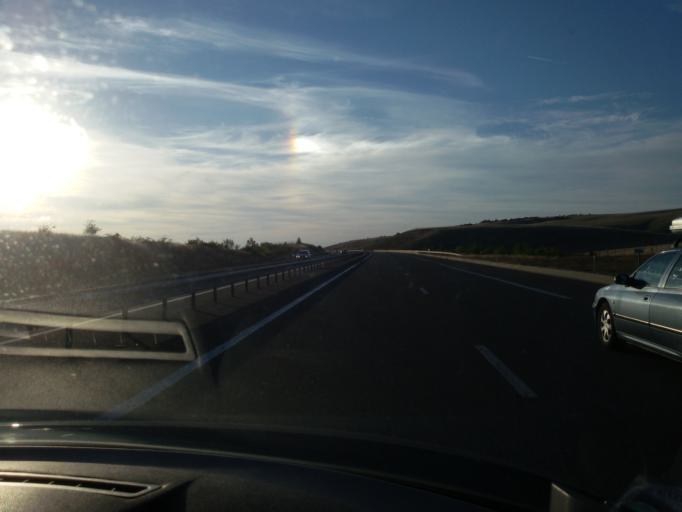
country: FR
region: Midi-Pyrenees
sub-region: Departement de l'Aveyron
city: La Cavalerie
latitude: 44.0232
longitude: 3.1207
